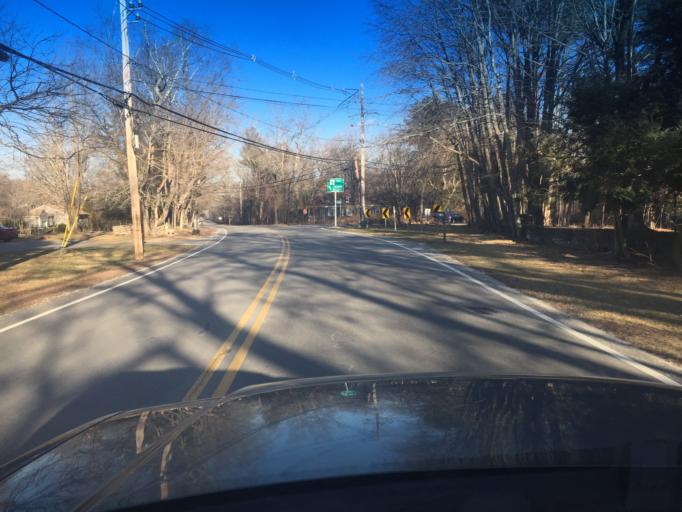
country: US
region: Massachusetts
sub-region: Middlesex County
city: Sherborn
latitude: 42.2222
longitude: -71.3982
